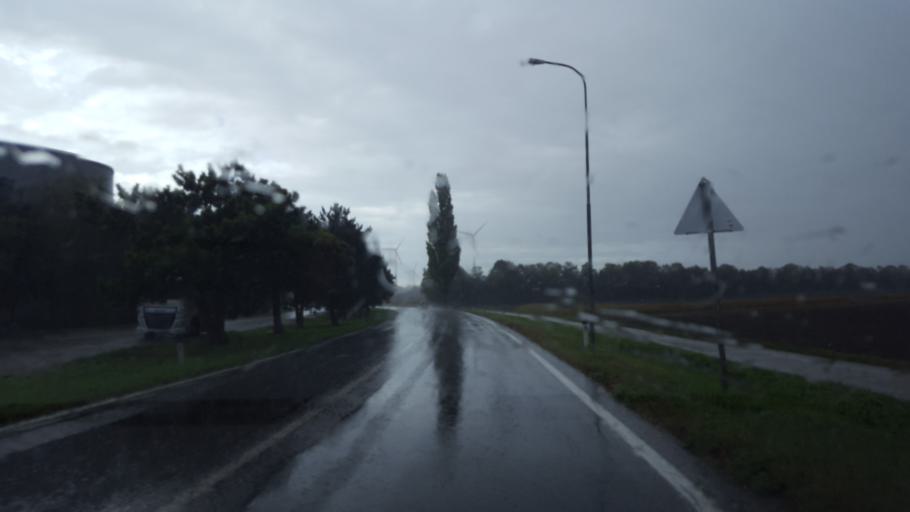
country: AT
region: Lower Austria
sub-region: Politischer Bezirk Bruck an der Leitha
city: Bruck an der Leitha
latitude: 48.0236
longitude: 16.7565
